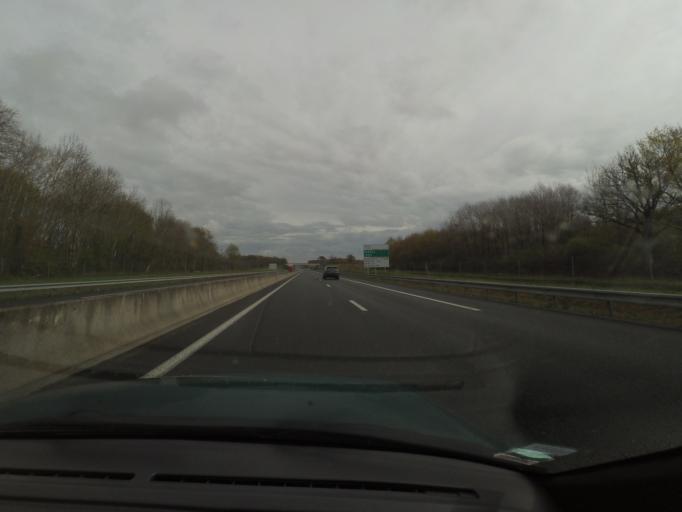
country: FR
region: Pays de la Loire
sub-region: Departement de Maine-et-Loire
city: Saint-Lambert-la-Potherie
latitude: 47.4724
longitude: -0.6797
